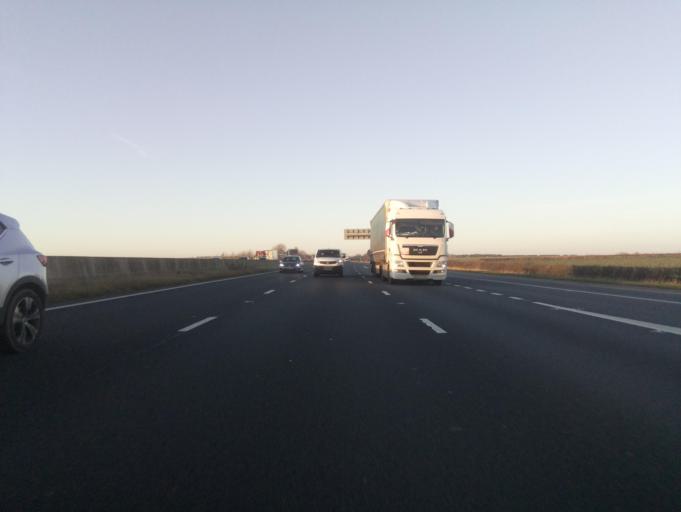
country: GB
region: England
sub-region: North Yorkshire
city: Boroughbridge
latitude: 54.1548
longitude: -1.4405
